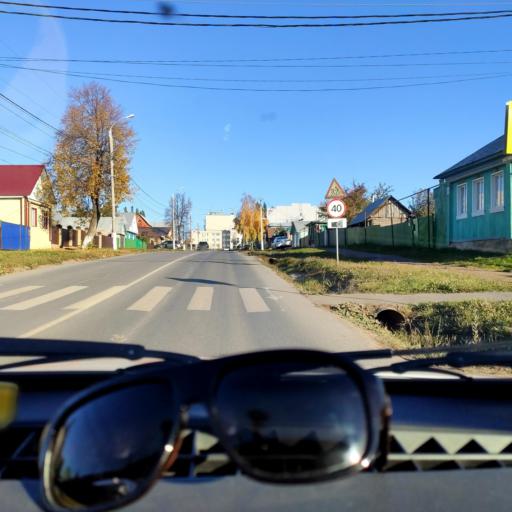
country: RU
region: Bashkortostan
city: Blagoveshchensk
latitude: 55.0439
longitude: 55.9601
